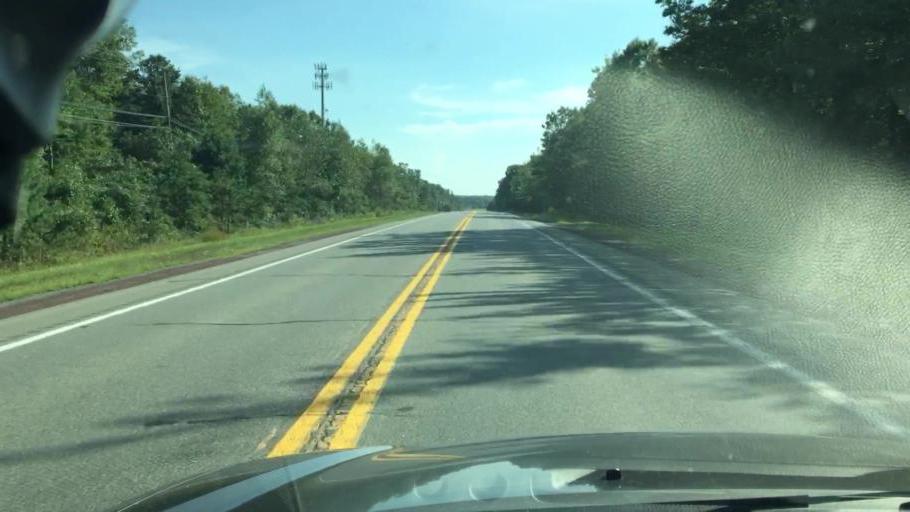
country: US
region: Pennsylvania
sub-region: Carbon County
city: Towamensing Trails
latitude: 40.9432
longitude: -75.6544
